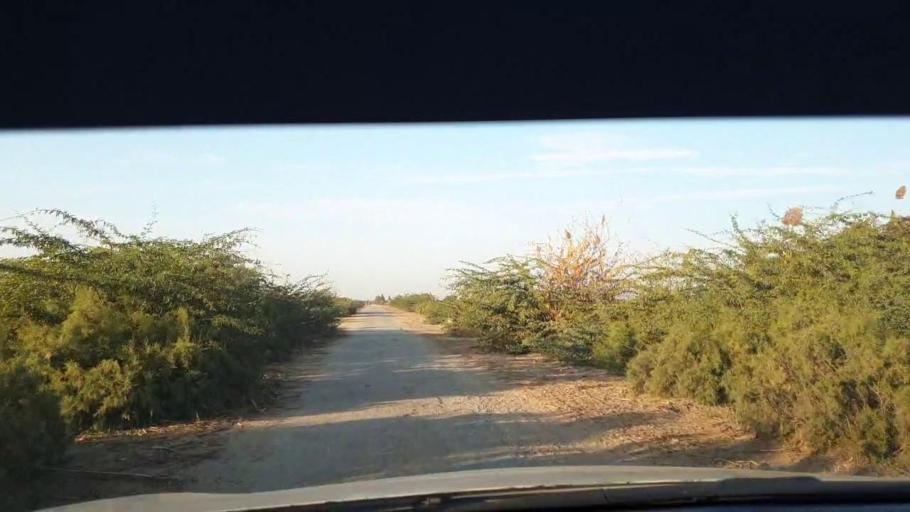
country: PK
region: Sindh
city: Berani
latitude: 25.8110
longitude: 68.8820
